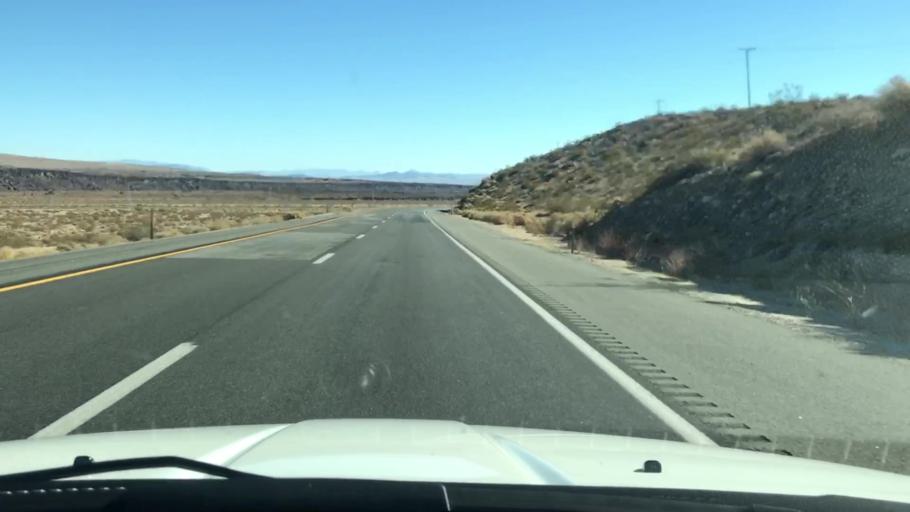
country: US
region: California
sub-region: Kern County
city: Inyokern
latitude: 35.8695
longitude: -117.8858
